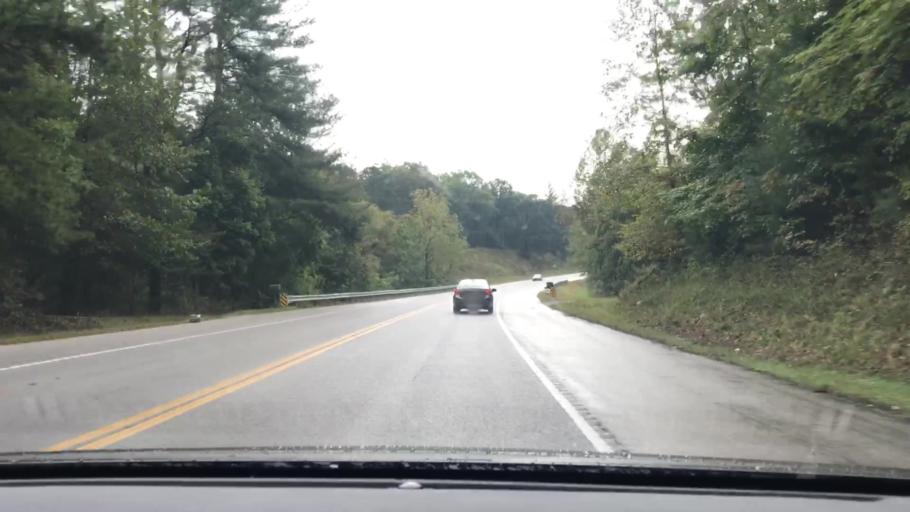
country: US
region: Tennessee
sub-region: Macon County
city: Red Boiling Springs
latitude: 36.5231
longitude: -85.8822
